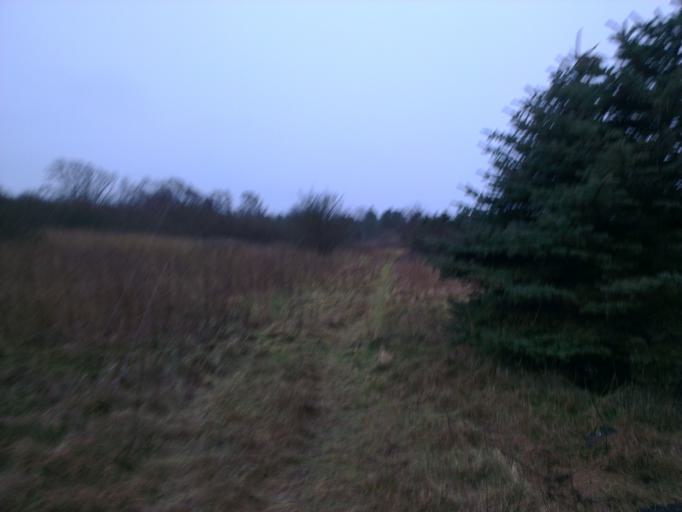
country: DK
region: Capital Region
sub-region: Frederikssund Kommune
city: Jaegerspris
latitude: 55.8434
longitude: 11.9644
